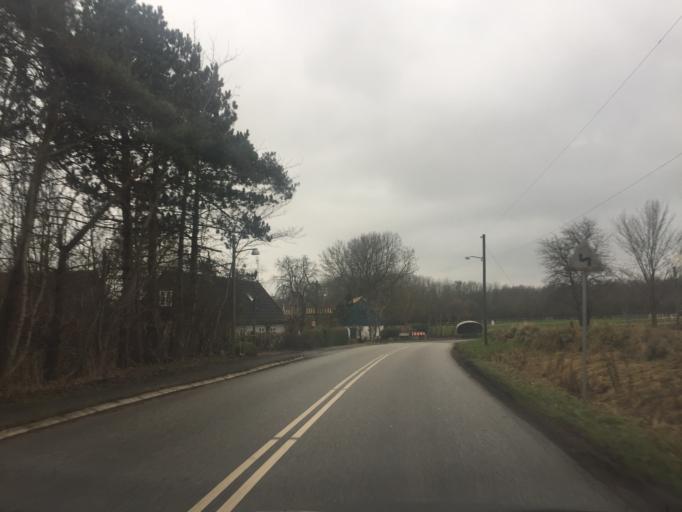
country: DK
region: Capital Region
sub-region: Albertslund Kommune
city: Albertslund
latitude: 55.6880
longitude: 12.3295
